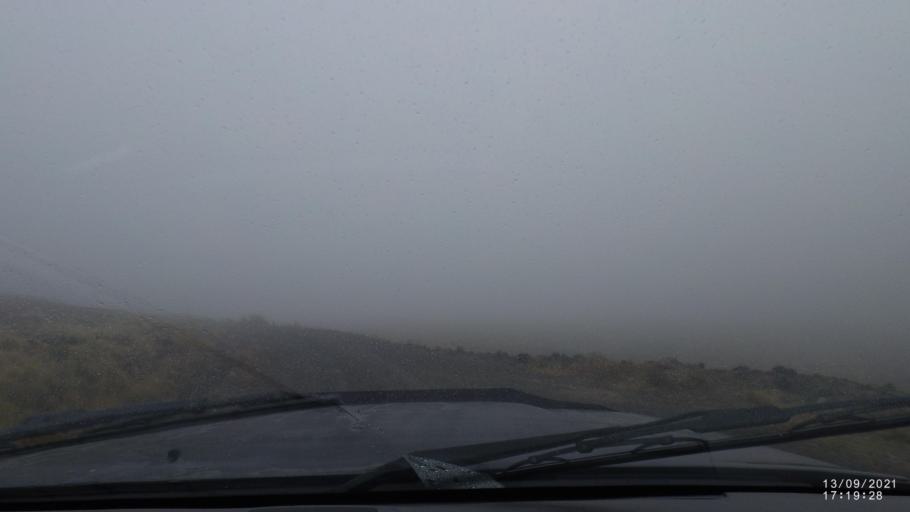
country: BO
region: Cochabamba
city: Colomi
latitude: -17.3498
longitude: -65.7620
